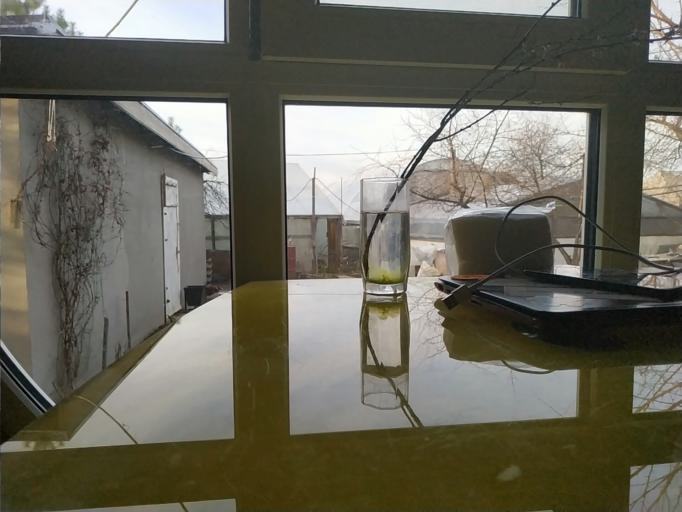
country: RU
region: Republic of Karelia
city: Suoyarvi
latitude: 62.1122
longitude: 32.1584
